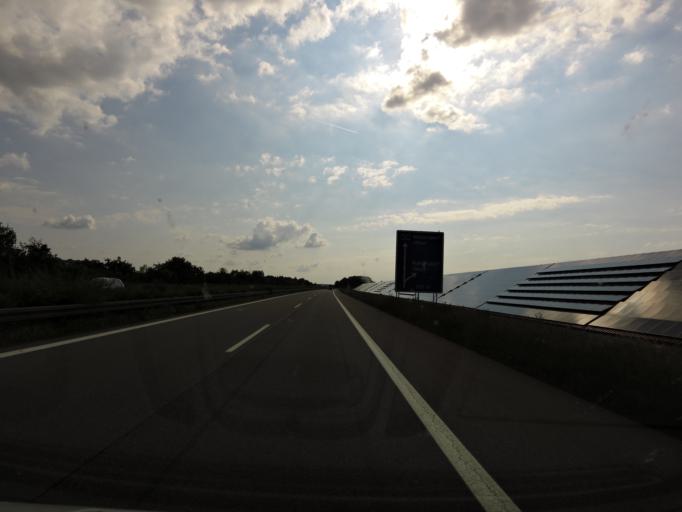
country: DE
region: Bavaria
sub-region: Lower Bavaria
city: Wallersdorf
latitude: 48.7488
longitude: 12.7525
